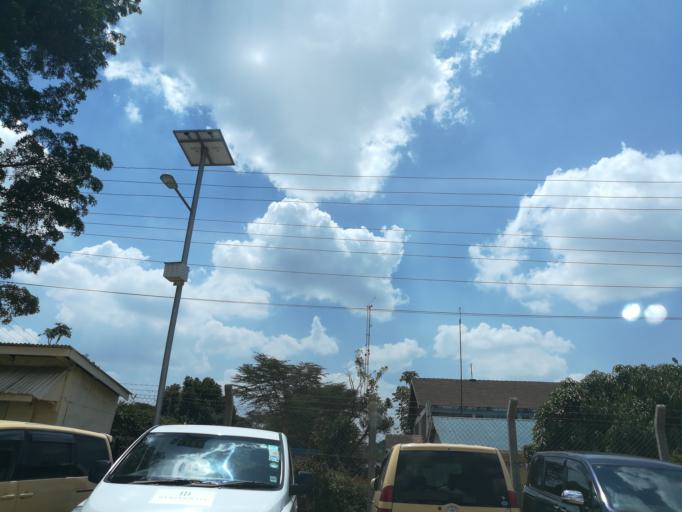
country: KE
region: Nairobi Area
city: Nairobi
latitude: -1.3186
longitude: 36.8161
